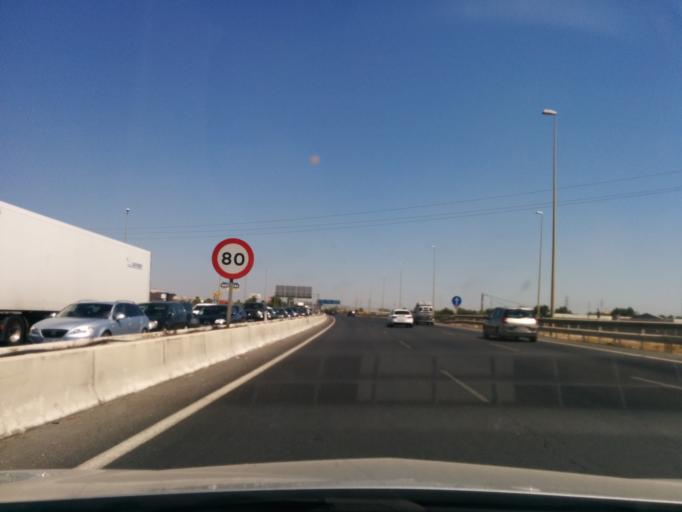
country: ES
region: Andalusia
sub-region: Provincia de Sevilla
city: Tomares
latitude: 37.3755
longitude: -6.0269
